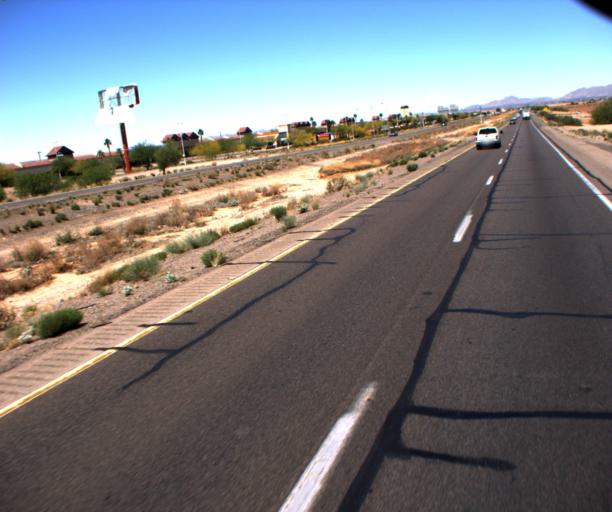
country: US
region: Arizona
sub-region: Pinal County
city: Arizona City
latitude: 32.8359
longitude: -111.6858
